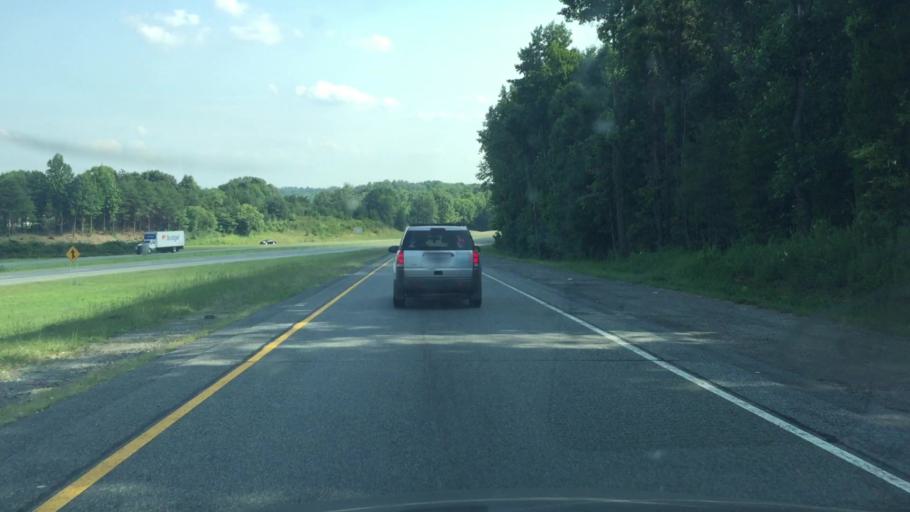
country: US
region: North Carolina
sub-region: Rockingham County
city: Reidsville
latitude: 36.3596
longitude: -79.6288
